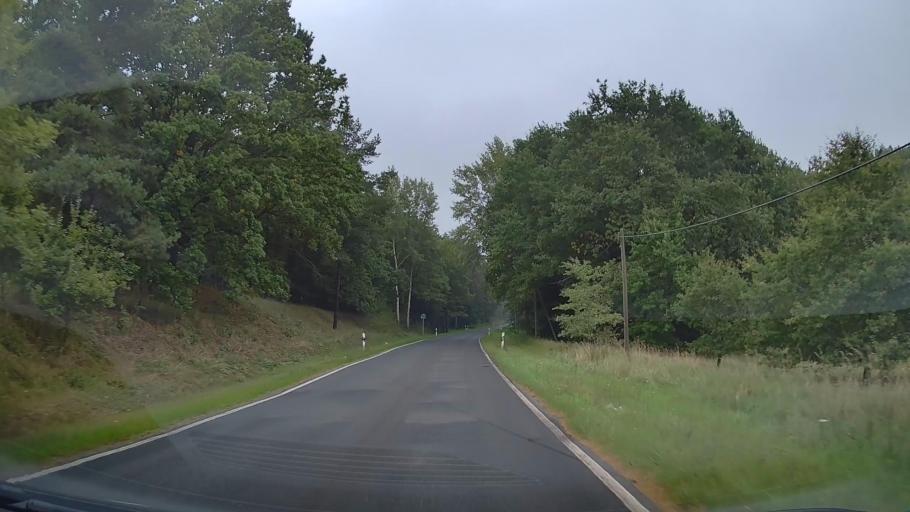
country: DE
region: Mecklenburg-Vorpommern
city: Hornstorf
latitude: 53.9489
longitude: 11.5729
